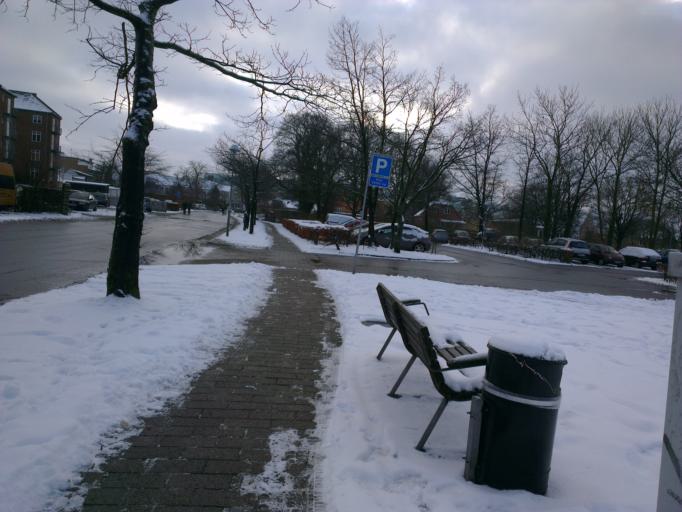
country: DK
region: Capital Region
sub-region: Frederikssund Kommune
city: Frederikssund
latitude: 55.8383
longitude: 12.0623
